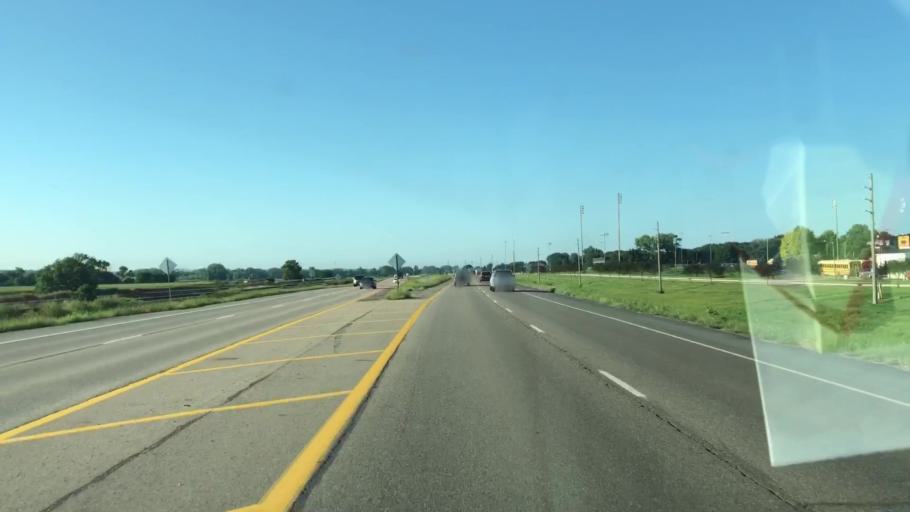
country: US
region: Iowa
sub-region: Woodbury County
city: Sioux City
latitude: 42.6234
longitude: -96.2929
